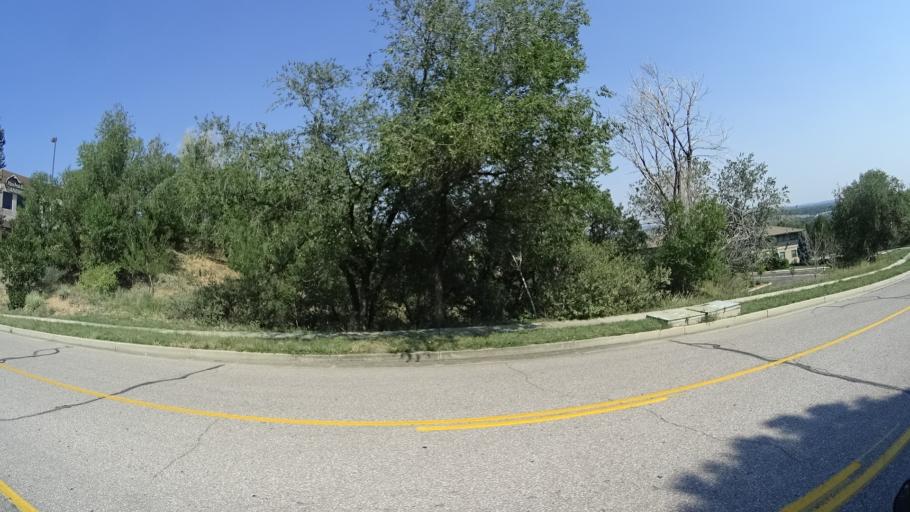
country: US
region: Colorado
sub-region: El Paso County
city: Stratmoor
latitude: 38.7944
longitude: -104.8130
